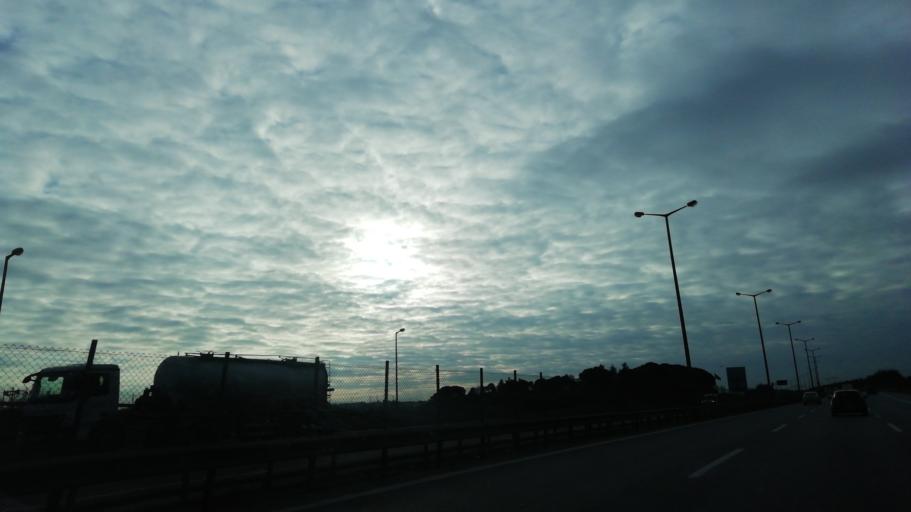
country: TR
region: Istanbul
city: Icmeler
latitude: 40.9237
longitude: 29.3507
